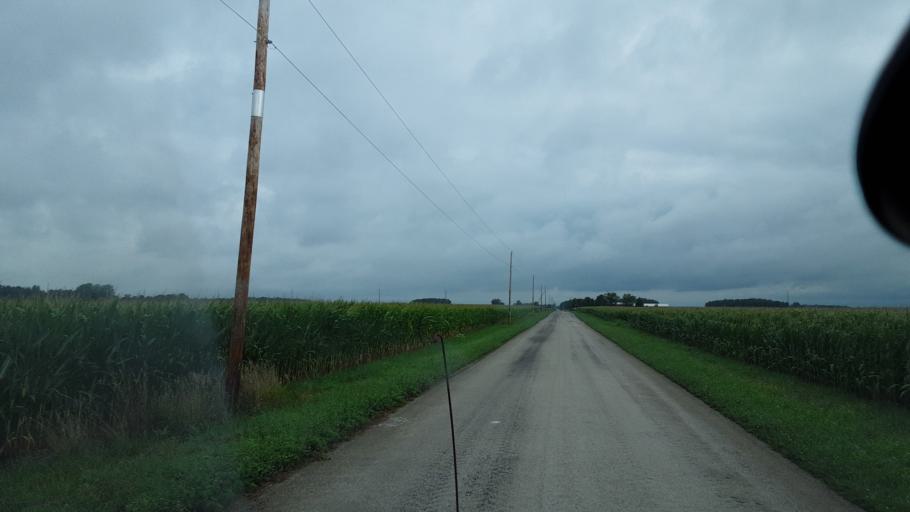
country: US
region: Indiana
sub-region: Allen County
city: Monroeville
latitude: 40.9109
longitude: -84.8425
